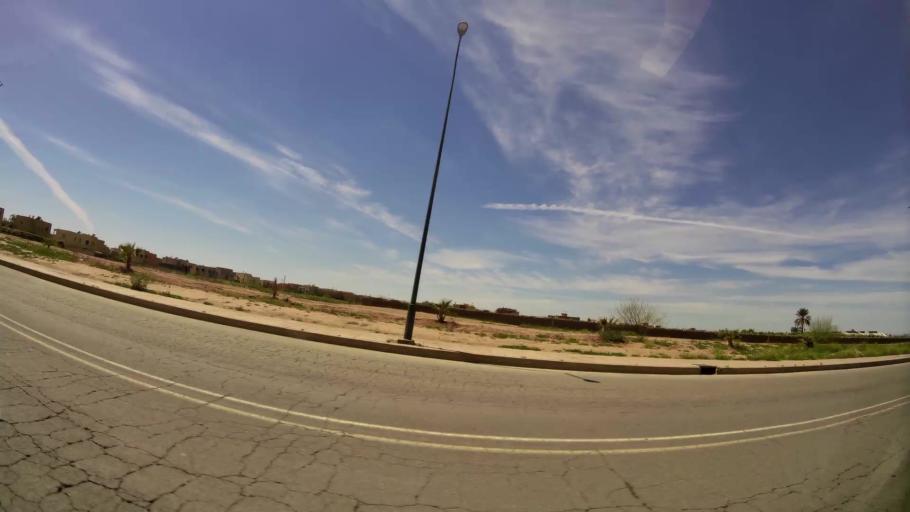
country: MA
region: Marrakech-Tensift-Al Haouz
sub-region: Marrakech
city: Marrakesh
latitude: 31.6504
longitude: -8.0674
